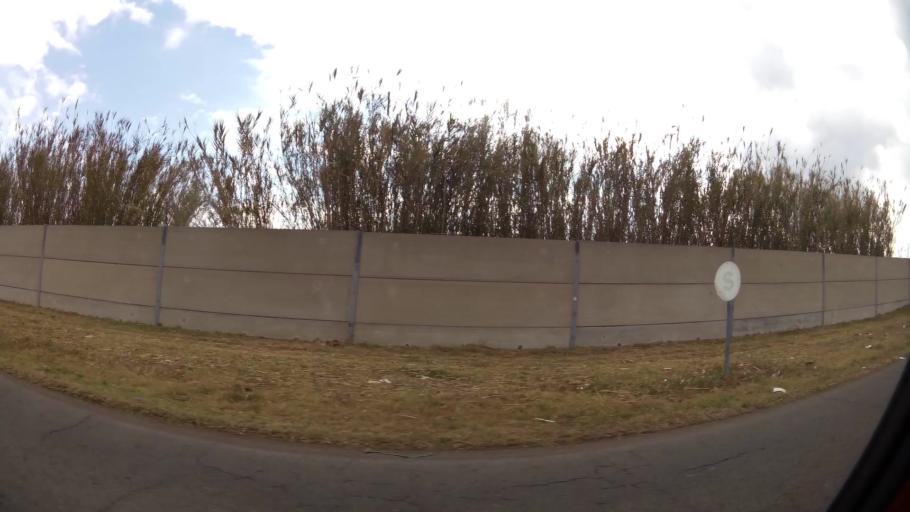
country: ZA
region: Gauteng
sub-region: Sedibeng District Municipality
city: Vanderbijlpark
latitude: -26.6771
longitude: 27.8181
